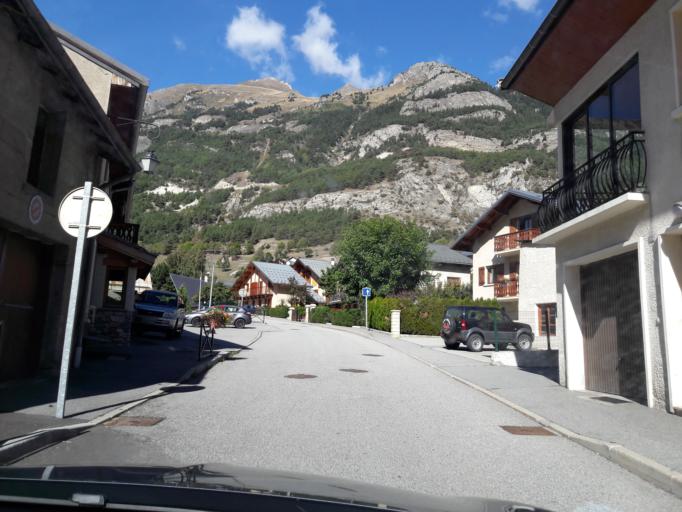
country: FR
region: Rhone-Alpes
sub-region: Departement de la Savoie
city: Modane
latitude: 45.2147
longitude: 6.7228
